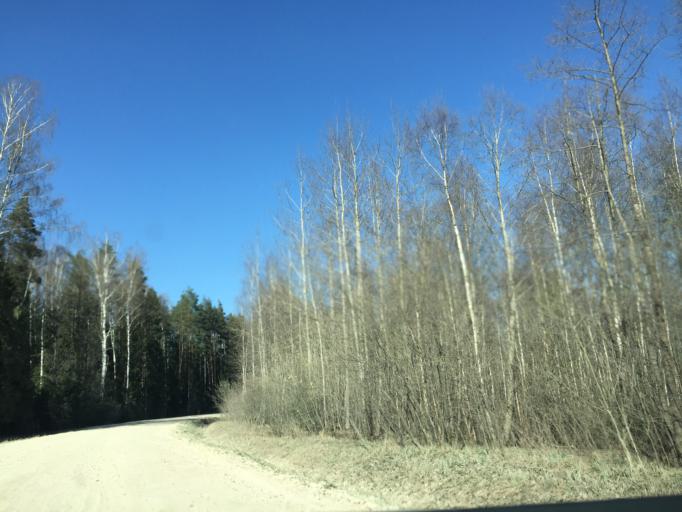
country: LV
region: Ropazu
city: Ropazi
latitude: 56.9358
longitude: 24.6916
